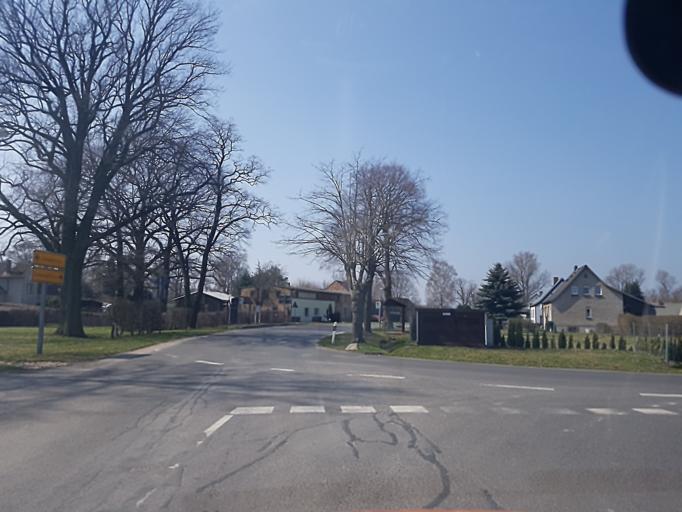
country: DE
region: Brandenburg
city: Forst
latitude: 51.6809
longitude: 14.5565
